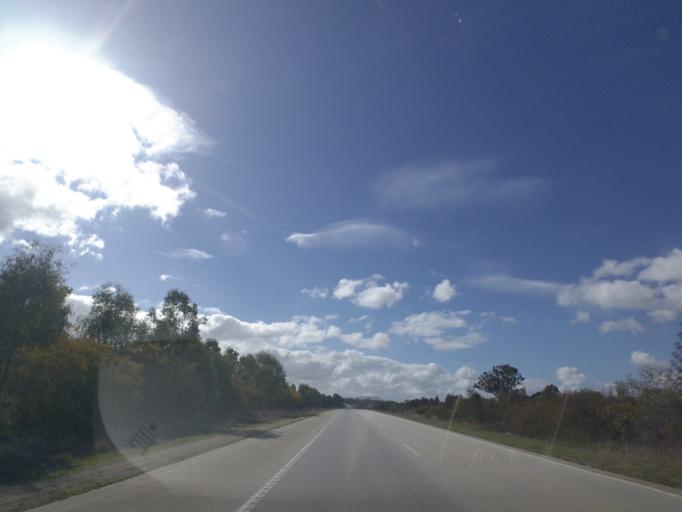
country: AU
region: New South Wales
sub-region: Albury Municipality
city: Lavington
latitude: -36.0104
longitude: 146.9880
